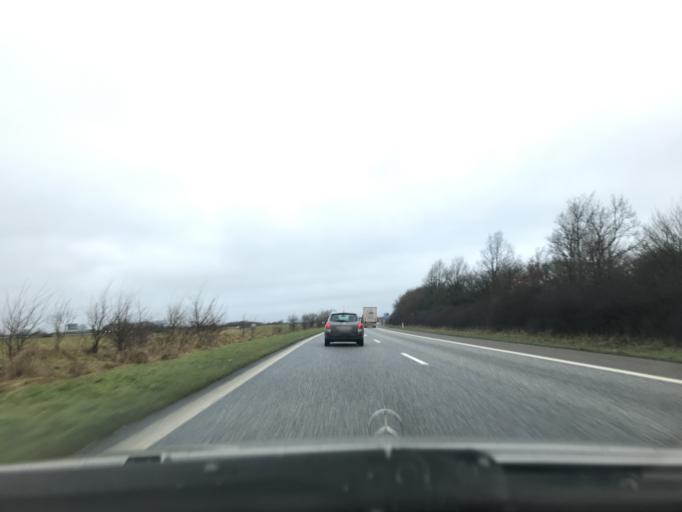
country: DK
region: South Denmark
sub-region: Aabenraa Kommune
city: Aabenraa
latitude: 55.0116
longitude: 9.3625
